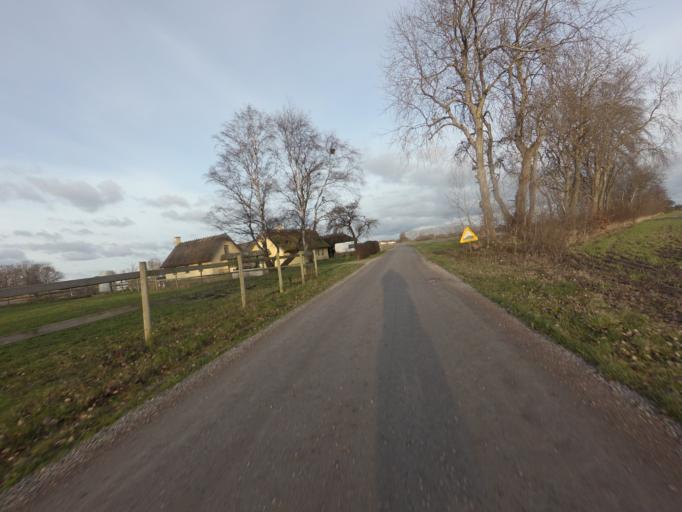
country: SE
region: Skane
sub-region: Hoganas Kommun
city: Hoganas
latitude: 56.1737
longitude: 12.5823
